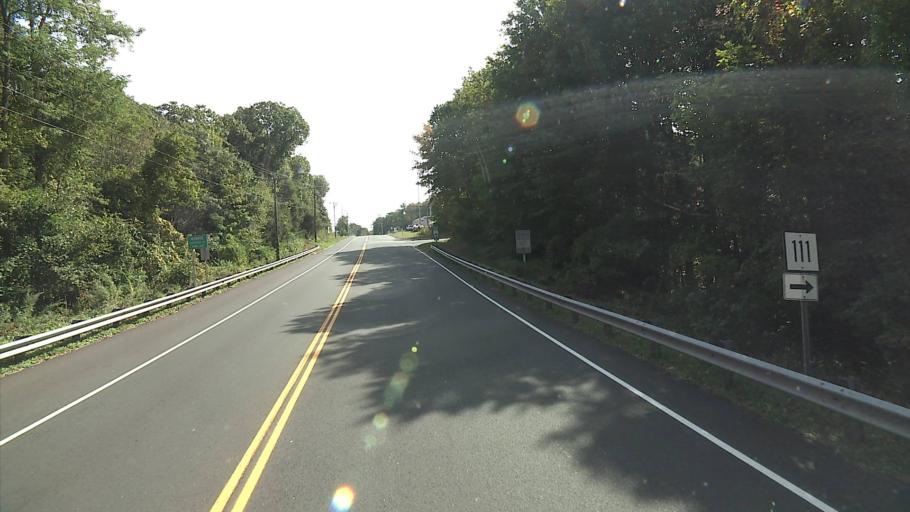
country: US
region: Connecticut
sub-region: New Haven County
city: Oxford
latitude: 41.3886
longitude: -73.1891
